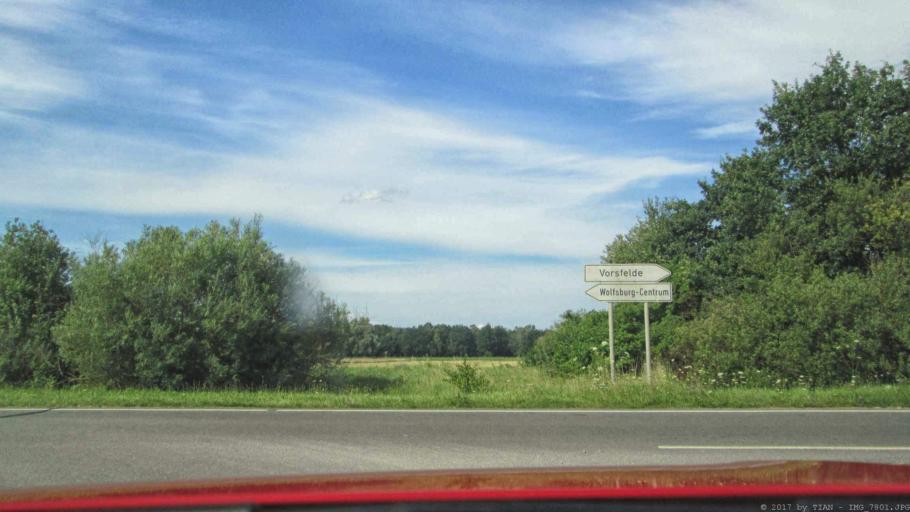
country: DE
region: Lower Saxony
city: Wolfsburg
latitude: 52.4262
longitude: 10.8299
